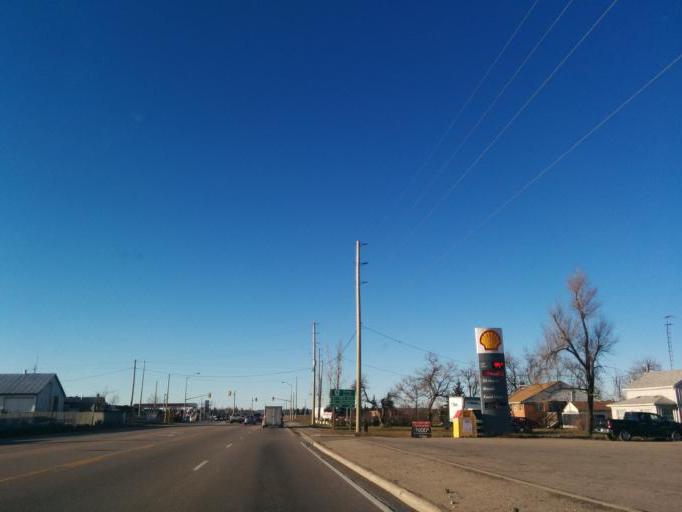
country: CA
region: Ontario
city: Brampton
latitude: 43.7723
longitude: -79.8766
